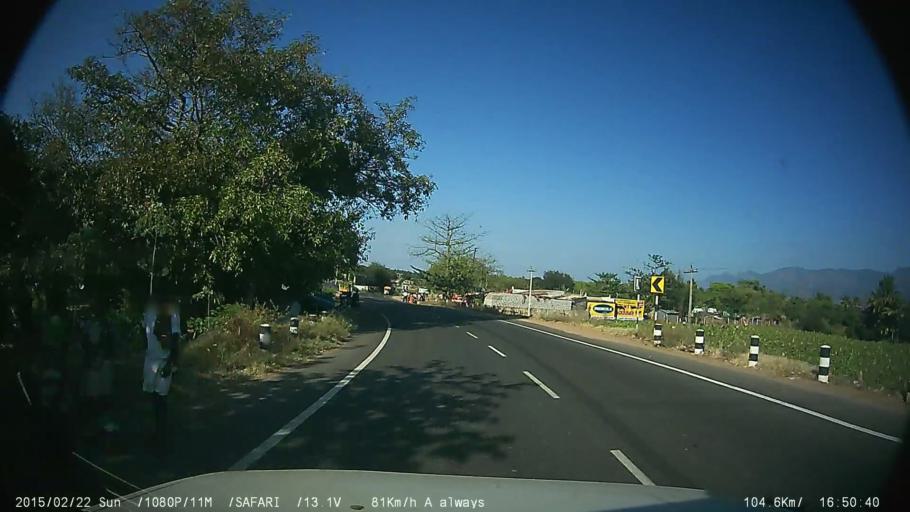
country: IN
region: Tamil Nadu
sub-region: Theni
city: Gudalur
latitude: 9.6436
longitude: 77.2121
